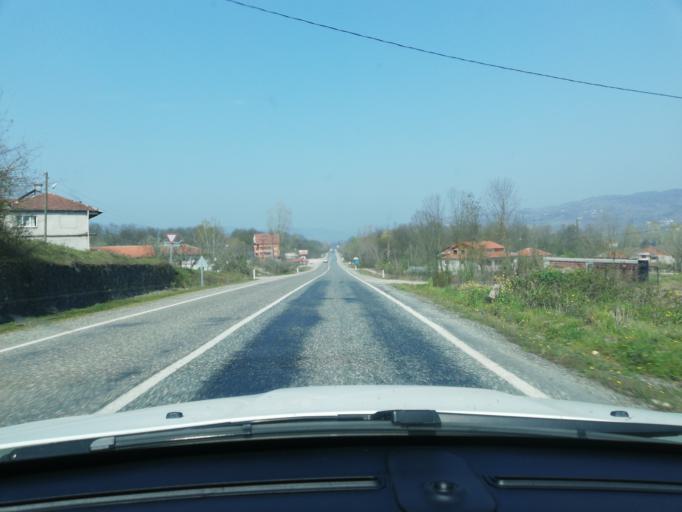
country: TR
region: Zonguldak
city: Gokcebey
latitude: 41.2899
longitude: 32.1386
